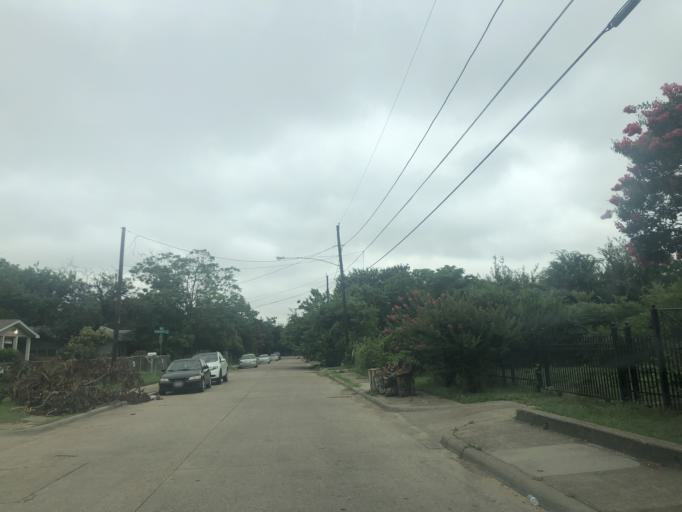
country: US
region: Texas
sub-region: Dallas County
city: Dallas
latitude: 32.7763
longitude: -96.8498
